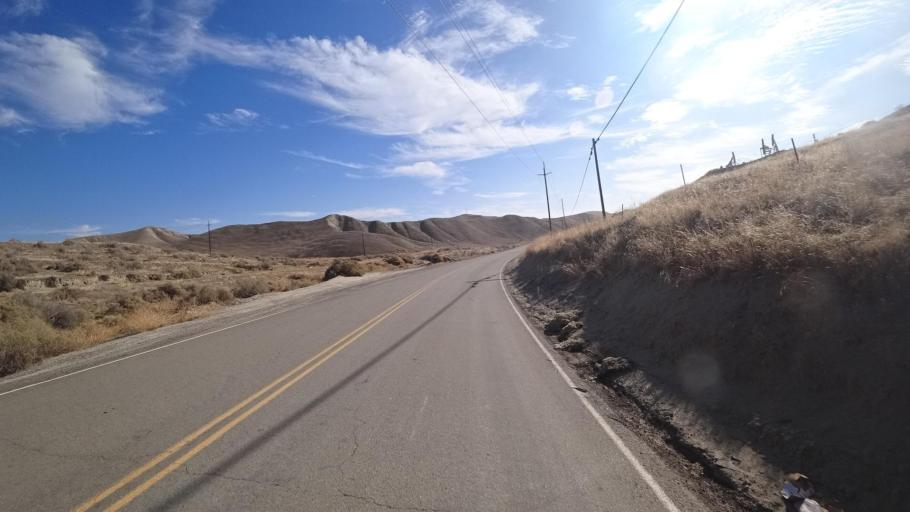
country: US
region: California
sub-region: Kern County
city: Oildale
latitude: 35.5662
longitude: -118.9567
